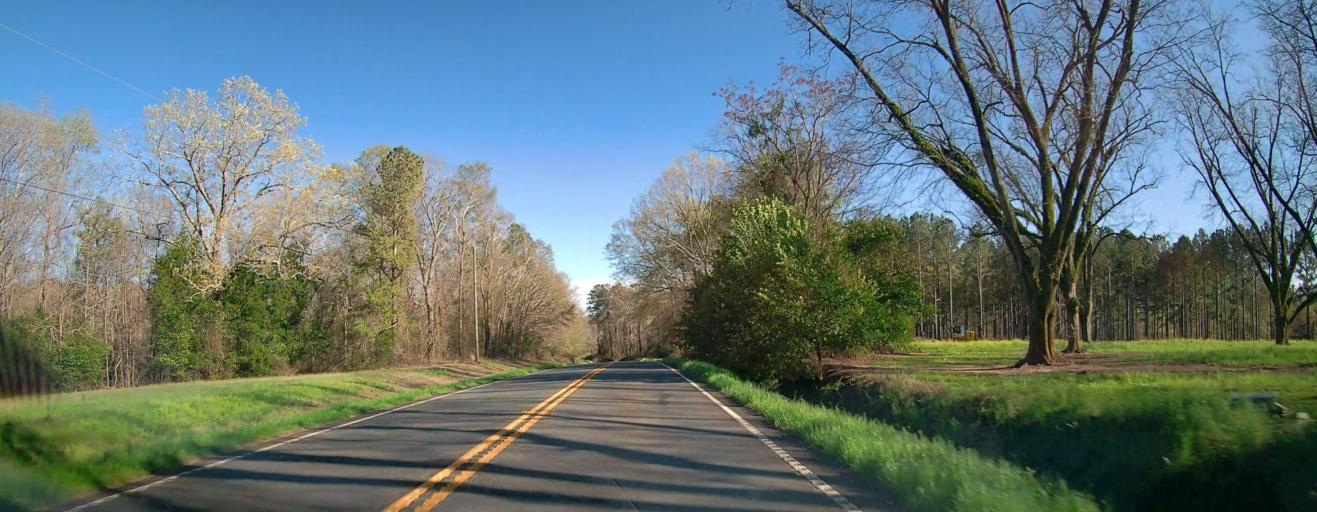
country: US
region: Georgia
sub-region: Macon County
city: Marshallville
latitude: 32.4517
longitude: -83.9113
